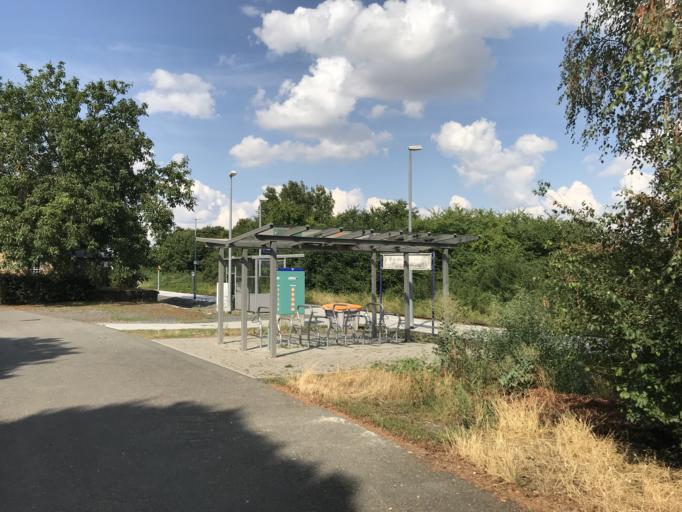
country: DE
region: Hesse
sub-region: Regierungsbezirk Darmstadt
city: Wolfersheim
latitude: 50.3785
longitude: 8.8113
